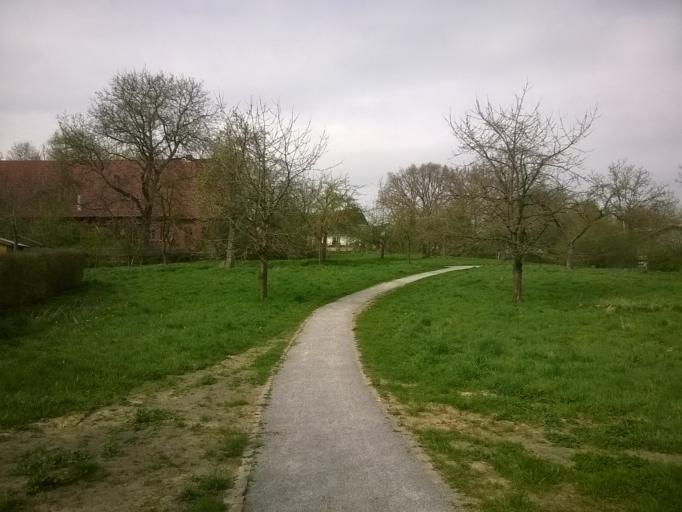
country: DE
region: North Rhine-Westphalia
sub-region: Regierungsbezirk Detmold
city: Hiddenhausen
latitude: 52.1432
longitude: 8.6169
